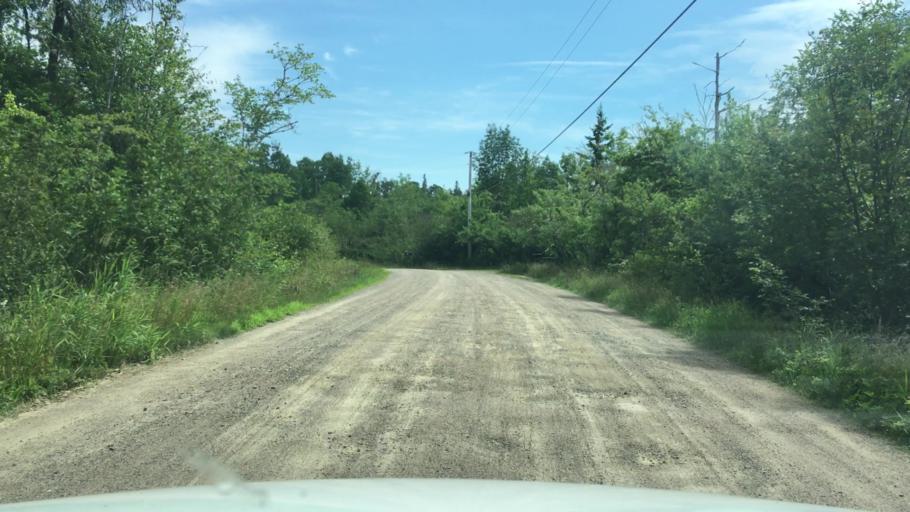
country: CA
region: New Brunswick
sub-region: Charlotte County
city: Saint Andrews
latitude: 45.0355
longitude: -67.1143
